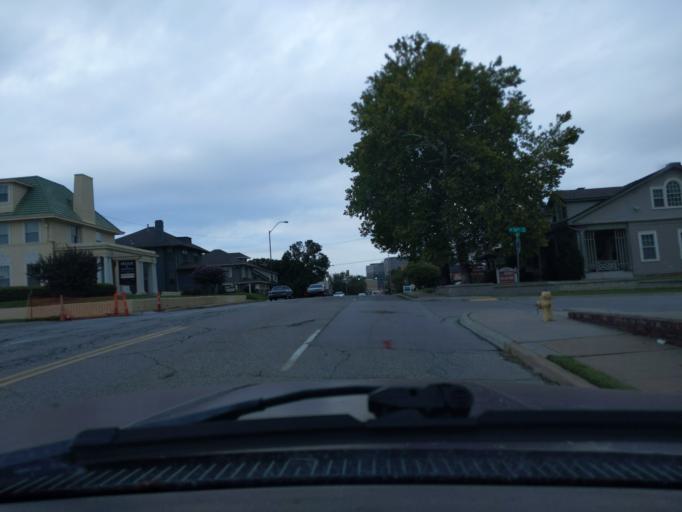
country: US
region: Oklahoma
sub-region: Tulsa County
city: Tulsa
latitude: 36.1395
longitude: -95.9923
